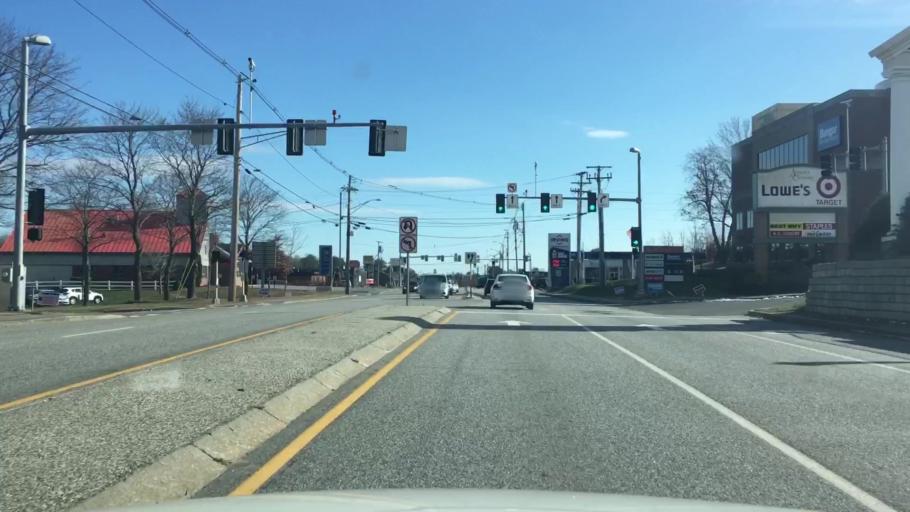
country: US
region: Maine
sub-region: Kennebec County
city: Augusta
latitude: 44.3157
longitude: -69.8057
